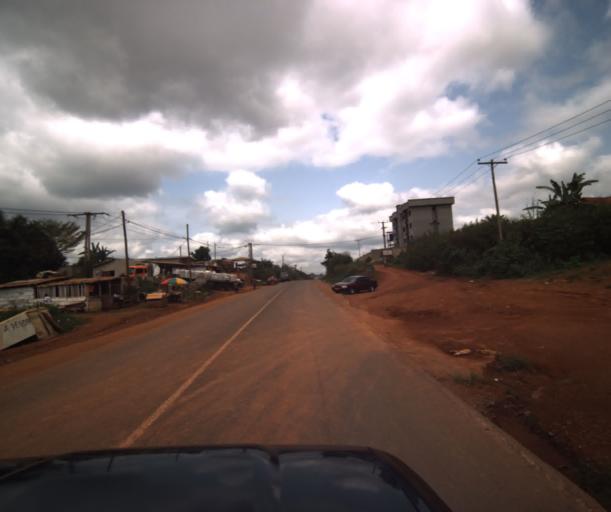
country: CM
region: Centre
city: Yaounde
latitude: 3.7945
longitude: 11.4901
